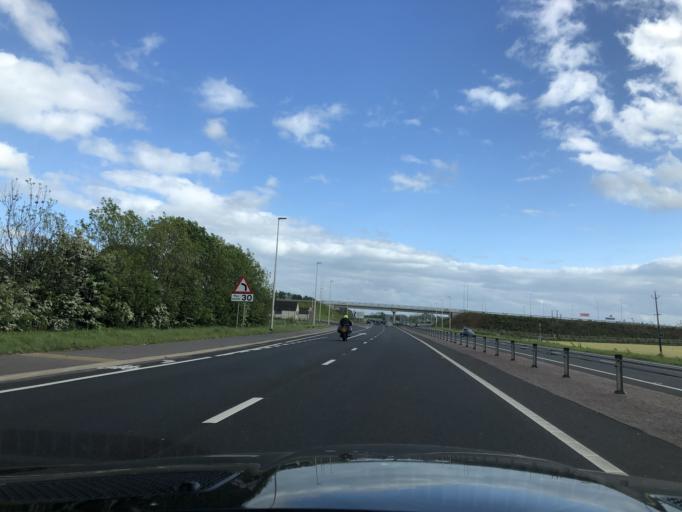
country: GB
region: Northern Ireland
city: Cullybackey
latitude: 54.9575
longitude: -6.3397
